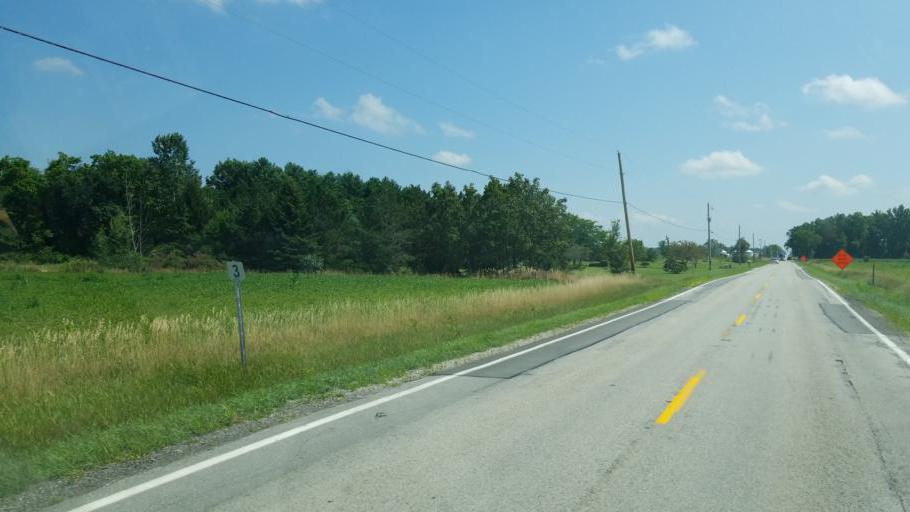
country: US
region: Ohio
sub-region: Huron County
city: Bellevue
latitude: 41.2175
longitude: -82.8386
